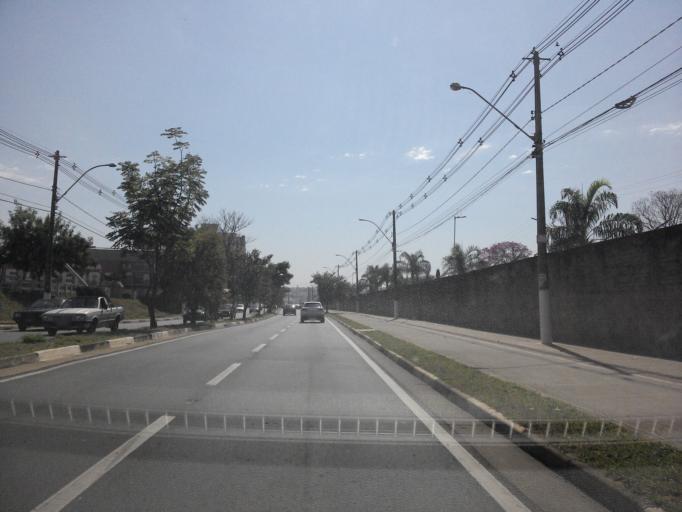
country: BR
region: Sao Paulo
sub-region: Hortolandia
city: Hortolandia
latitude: -22.8778
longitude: -47.2296
